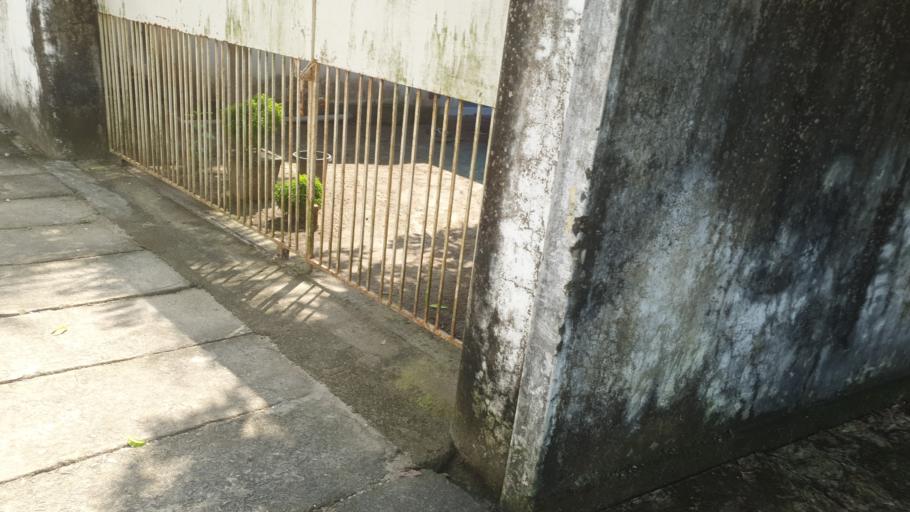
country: IN
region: Kerala
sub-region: Ernakulam
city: Cochin
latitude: 9.9737
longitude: 76.2405
